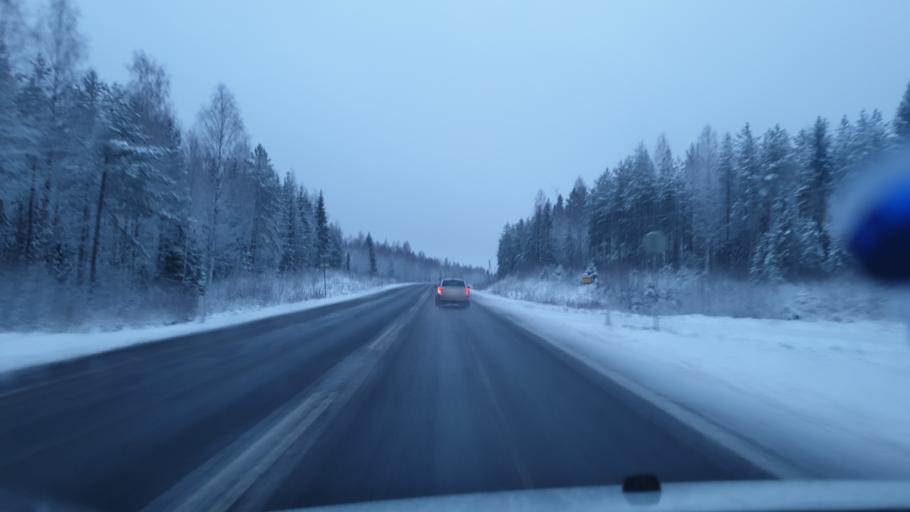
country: FI
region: Central Finland
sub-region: Saarijaervi-Viitasaari
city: Viitasaari
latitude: 63.1252
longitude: 25.7784
